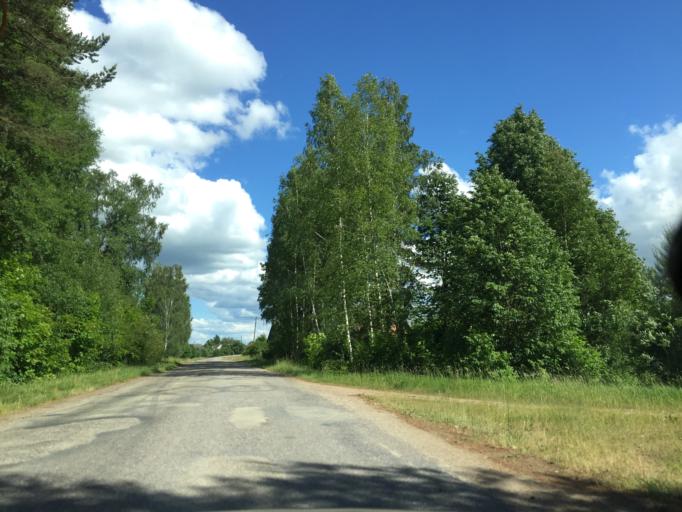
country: LT
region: Panevezys
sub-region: Birzai
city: Birzai
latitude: 56.3850
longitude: 24.6361
